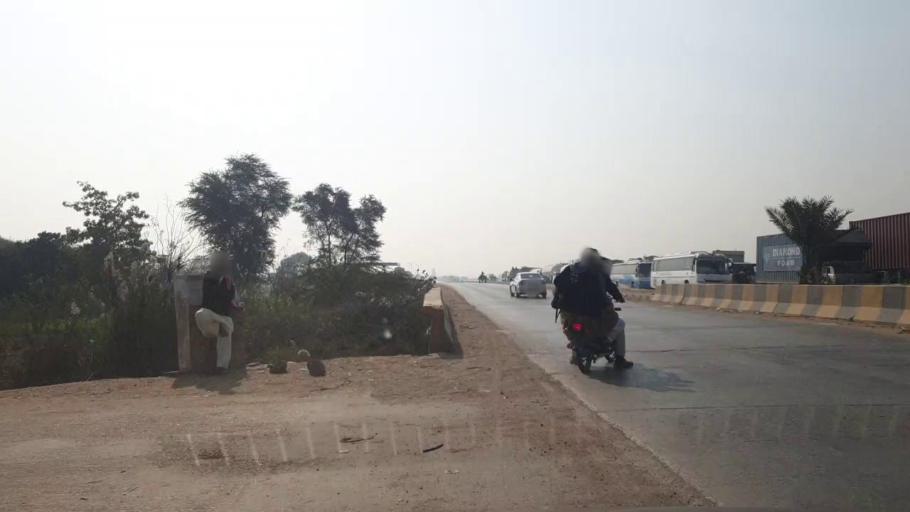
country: PK
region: Sindh
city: Hala
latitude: 25.9583
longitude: 68.3827
